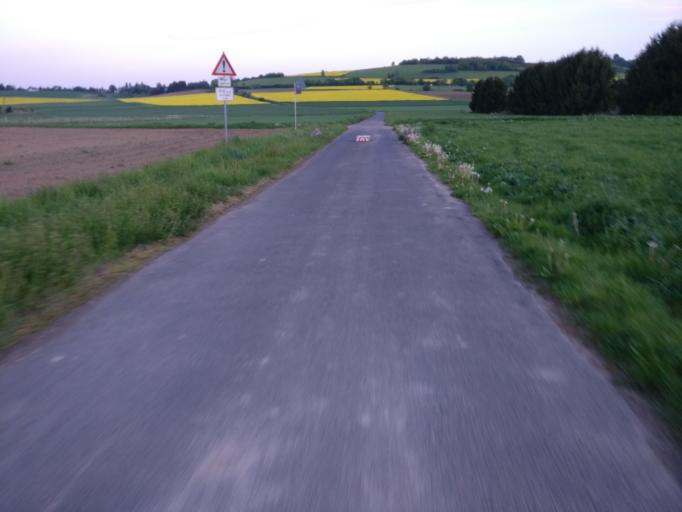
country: DE
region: Rheinland-Pfalz
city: Netzbach
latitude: 50.3586
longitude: 8.0975
